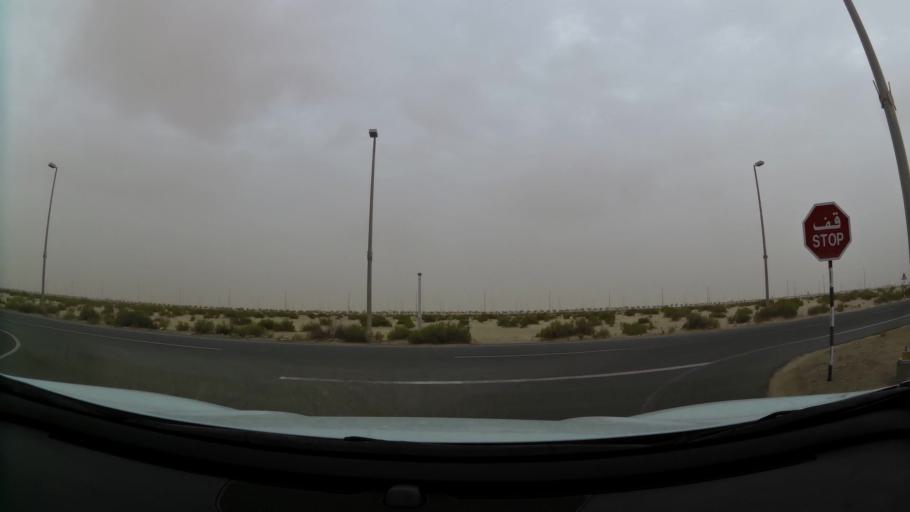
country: AE
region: Abu Dhabi
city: Abu Dhabi
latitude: 24.4207
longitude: 54.7045
